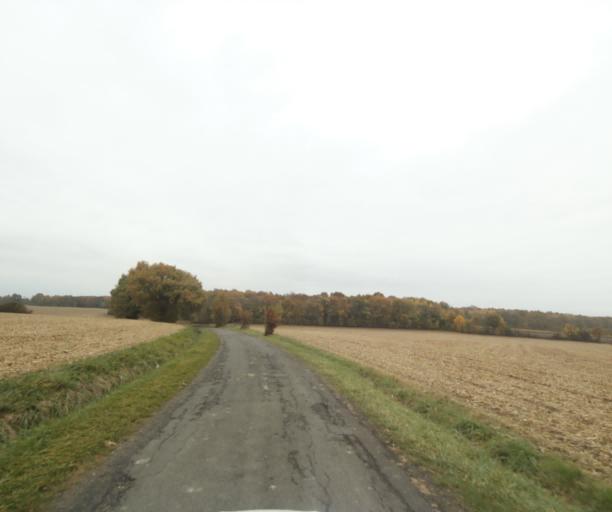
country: FR
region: Poitou-Charentes
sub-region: Departement de la Charente-Maritime
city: Saint-Georges-des-Coteaux
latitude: 45.7387
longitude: -0.6894
